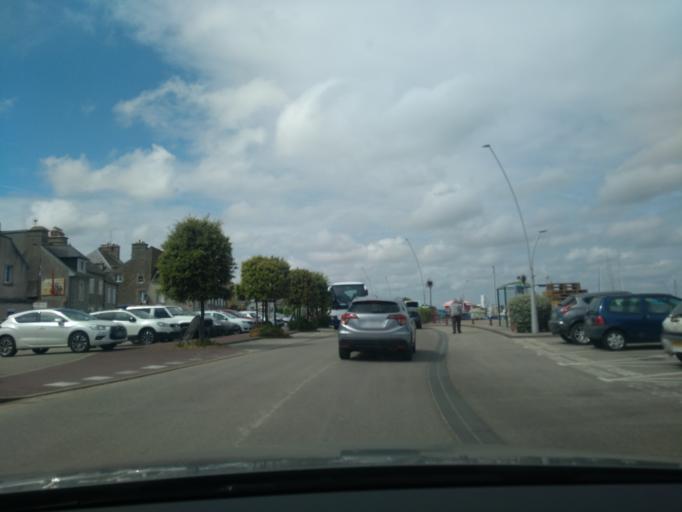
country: FR
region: Lower Normandy
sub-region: Departement de la Manche
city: Saint-Vaast-la-Hougue
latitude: 49.5886
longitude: -1.2661
